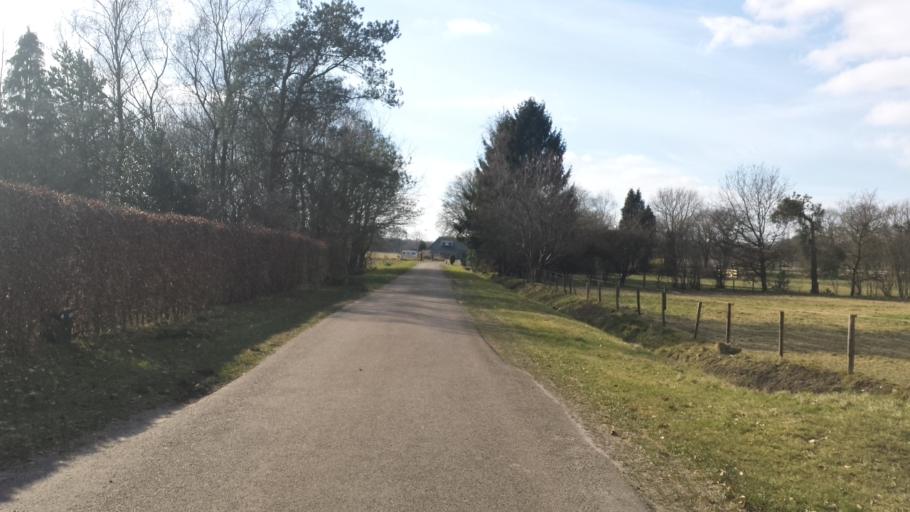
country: NL
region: Overijssel
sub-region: Gemeente Steenwijkerland
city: Tuk
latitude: 52.8128
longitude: 6.1023
